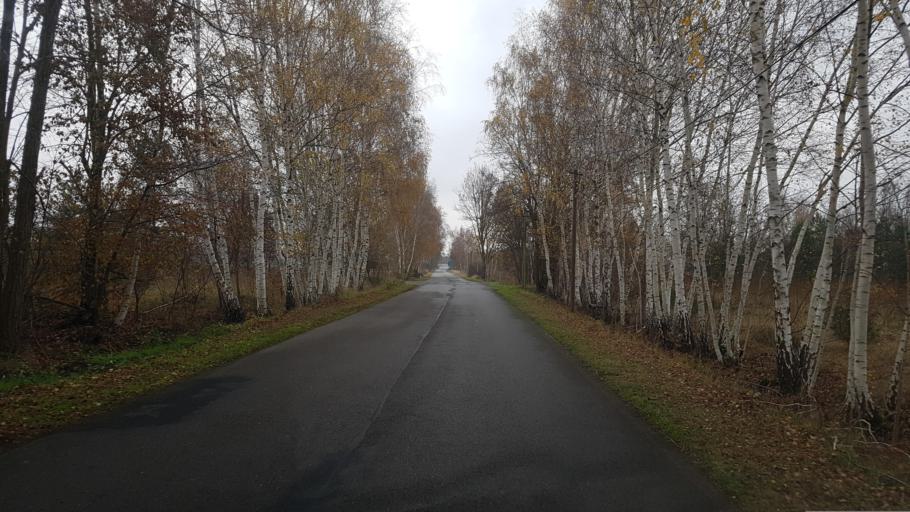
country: DE
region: Brandenburg
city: Lubbenau
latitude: 51.8356
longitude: 13.9058
